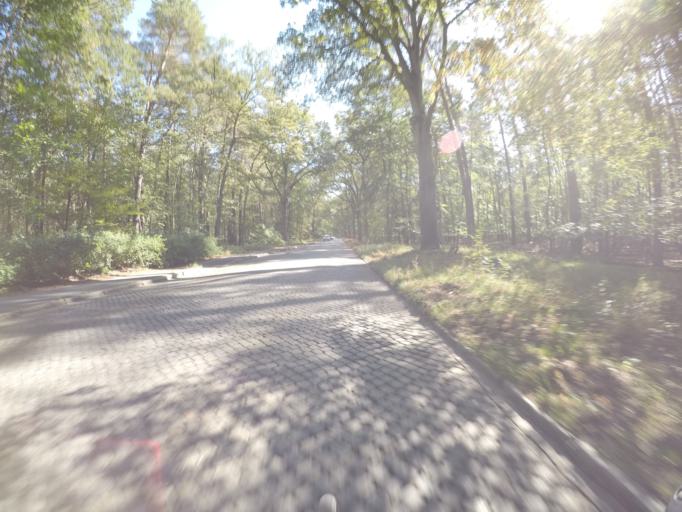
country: DE
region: Berlin
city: Falkenhagener Feld
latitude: 52.5768
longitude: 13.1813
